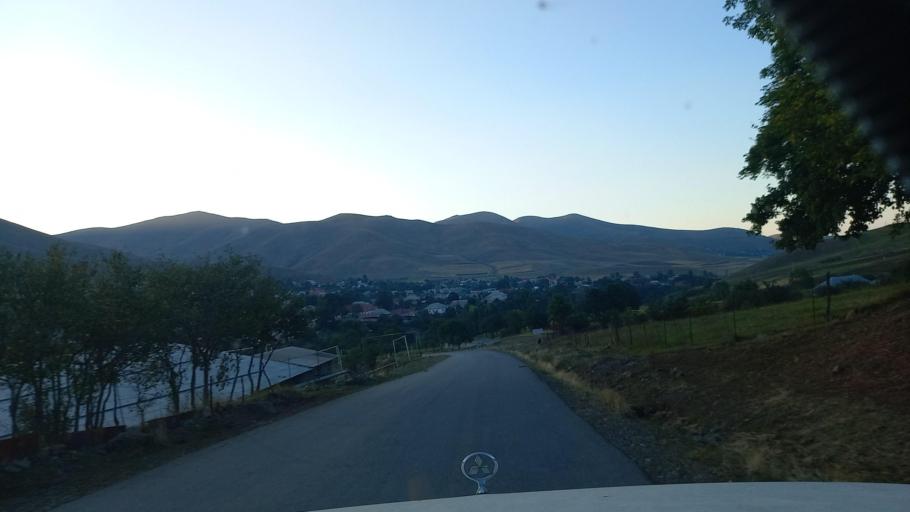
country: AZ
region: Tovuz
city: Cobansignaq
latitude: 40.6830
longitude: 45.7674
